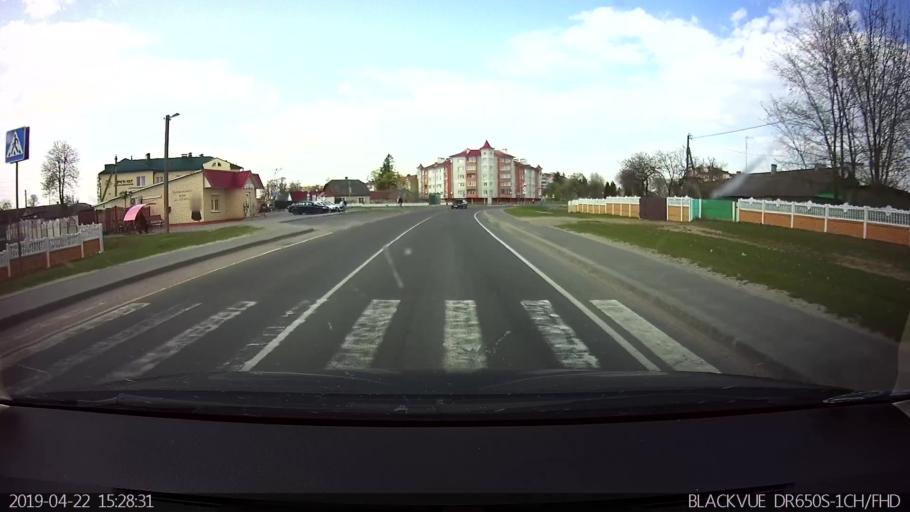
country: BY
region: Brest
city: Vysokaye
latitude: 52.3757
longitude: 23.3678
